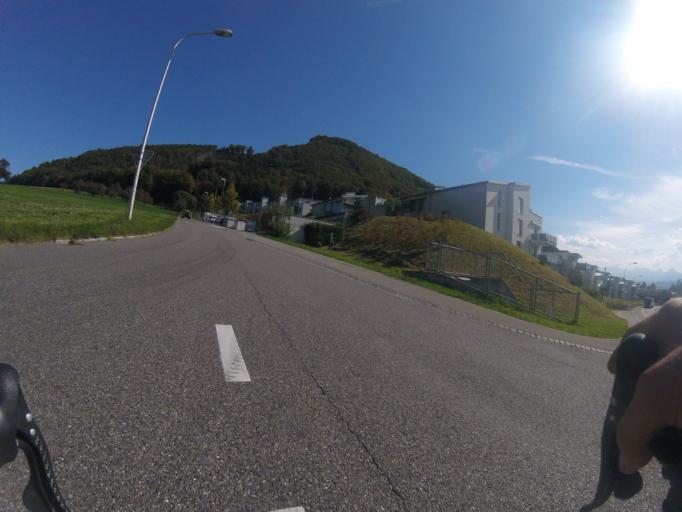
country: CH
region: Bern
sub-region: Bern-Mittelland District
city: Belp
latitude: 46.8821
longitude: 7.5056
